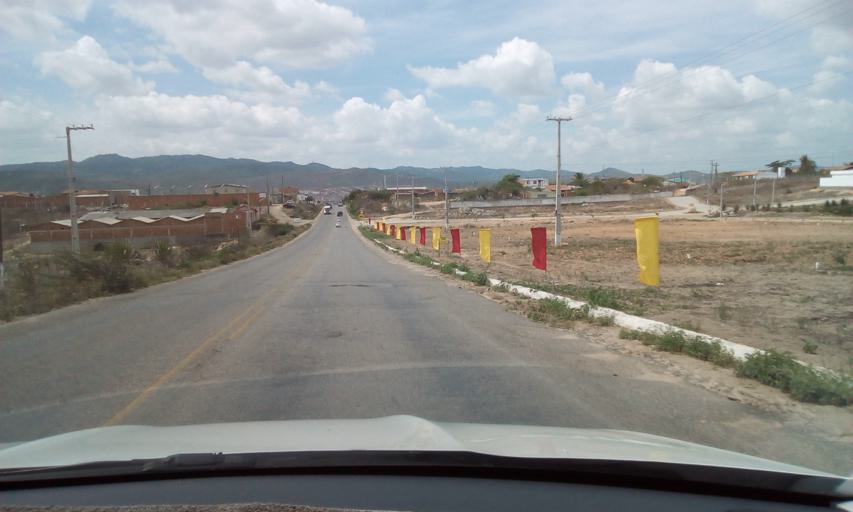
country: BR
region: Pernambuco
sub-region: Bezerros
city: Bezerros
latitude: -8.2576
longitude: -35.7572
